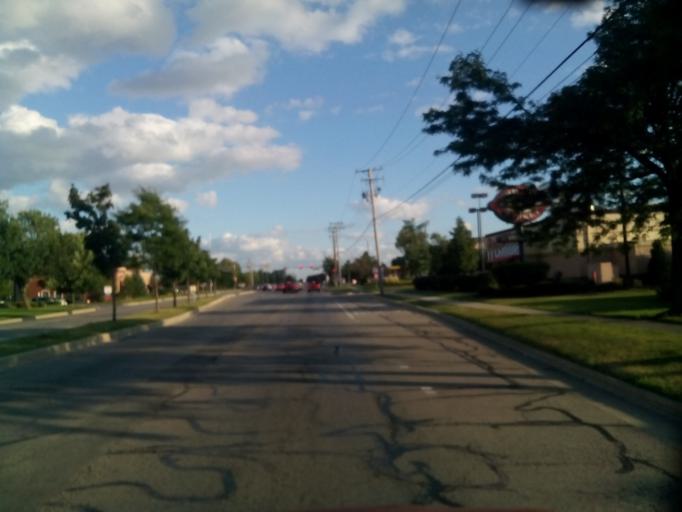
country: US
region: Illinois
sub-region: Will County
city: Bolingbrook
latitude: 41.7045
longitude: -88.1261
